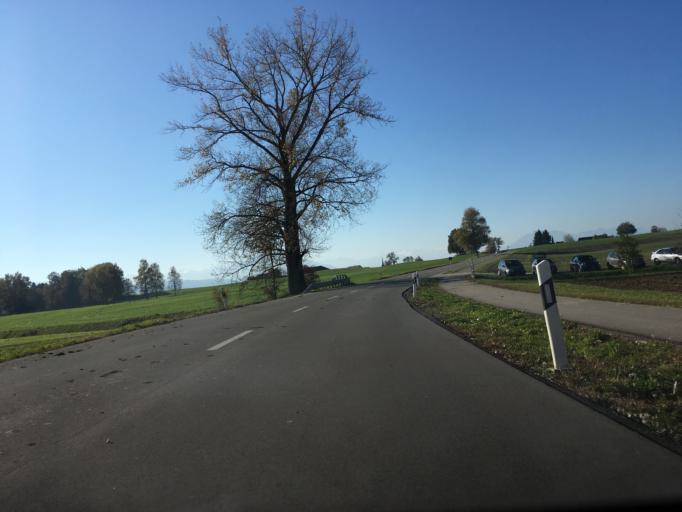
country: CH
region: Zurich
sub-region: Bezirk Affoltern
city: Hausen am Albis / Hausen (Dorf)
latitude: 47.2358
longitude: 8.5297
